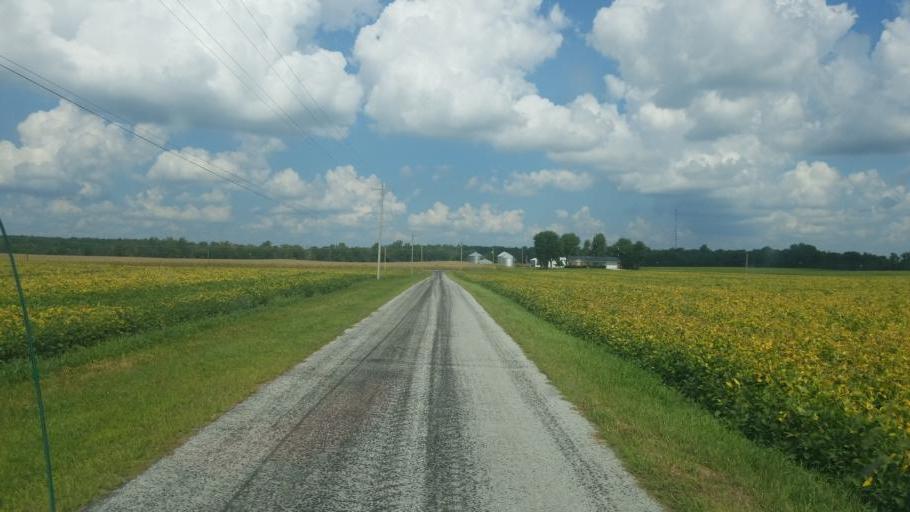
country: US
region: Ohio
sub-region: Hardin County
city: Kenton
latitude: 40.7015
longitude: -83.6386
